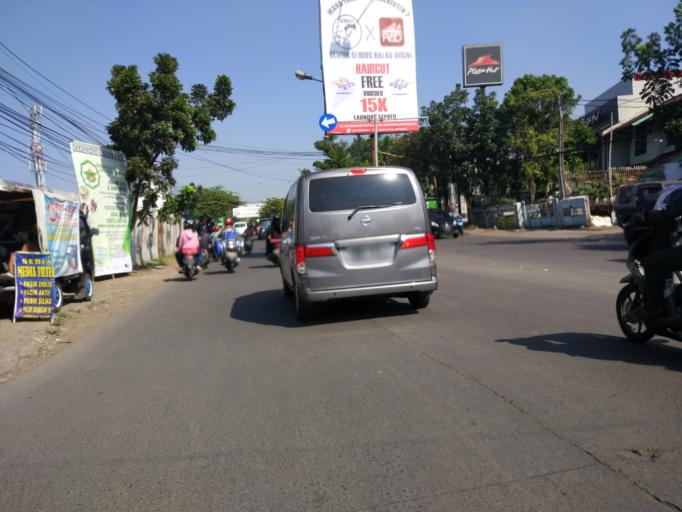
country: ID
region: West Java
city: Bandung
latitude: -6.9128
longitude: 107.6511
